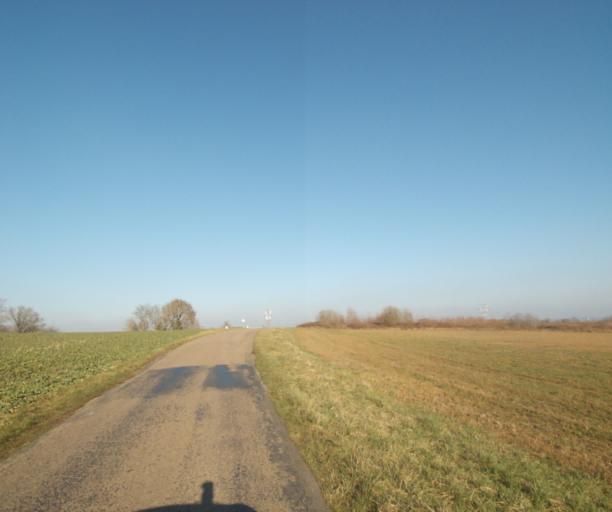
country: FR
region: Champagne-Ardenne
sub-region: Departement de la Haute-Marne
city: Chevillon
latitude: 48.5122
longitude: 5.0867
